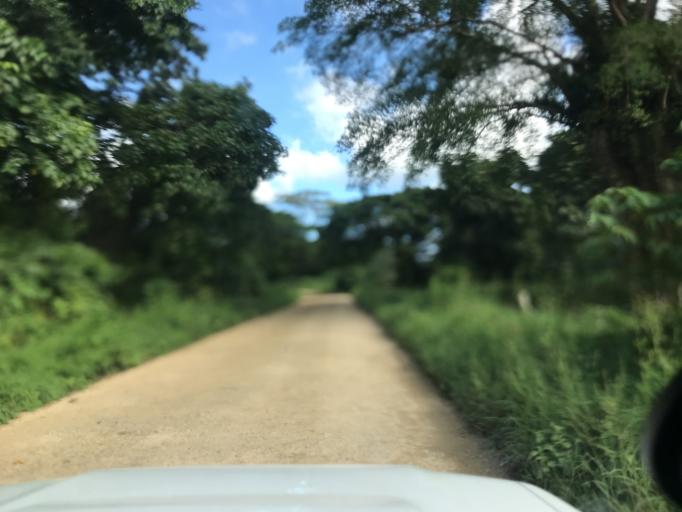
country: VU
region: Sanma
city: Luganville
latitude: -15.5100
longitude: 167.1212
